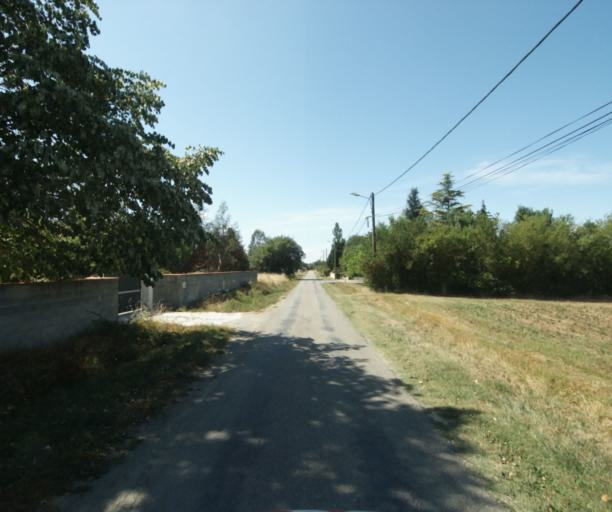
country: FR
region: Midi-Pyrenees
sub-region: Departement de la Haute-Garonne
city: Revel
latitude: 43.4827
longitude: 2.0067
